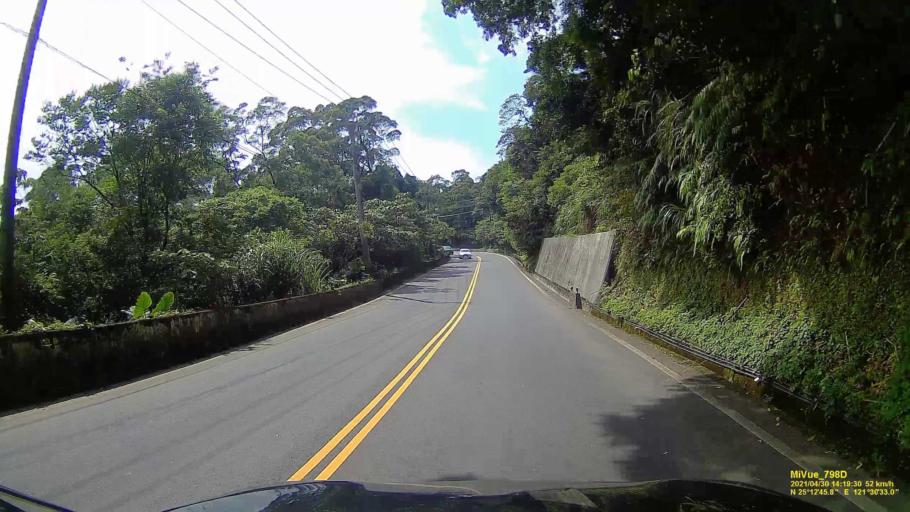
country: TW
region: Taipei
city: Taipei
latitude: 25.2128
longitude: 121.5089
